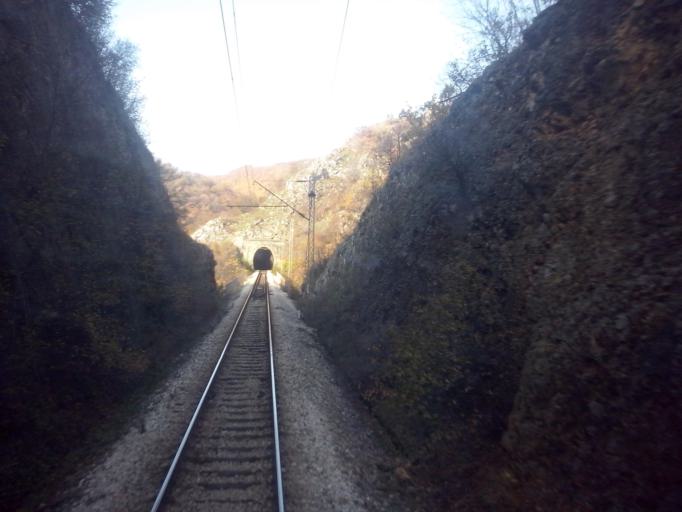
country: RS
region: Central Serbia
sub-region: Kolubarski Okrug
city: Valjevo
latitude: 44.2329
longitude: 19.8745
